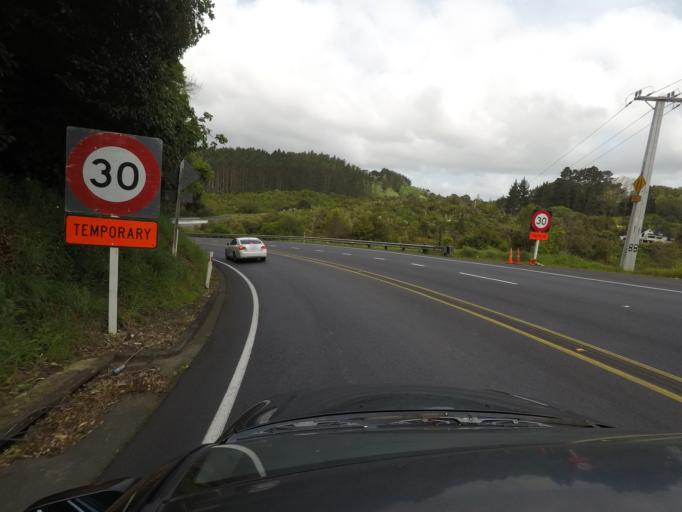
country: NZ
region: Auckland
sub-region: Auckland
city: Pakuranga
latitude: -36.9249
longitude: 174.9335
